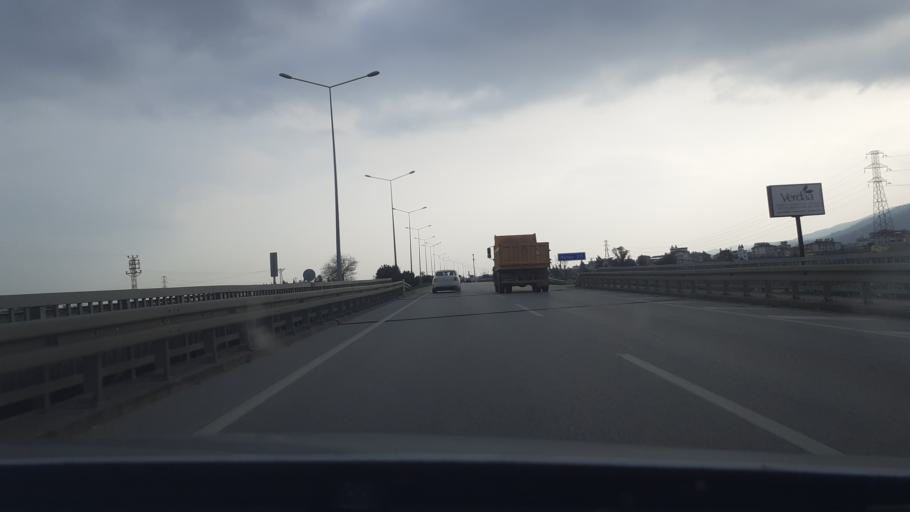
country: TR
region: Hatay
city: Serinyol
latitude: 36.3673
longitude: 36.2240
